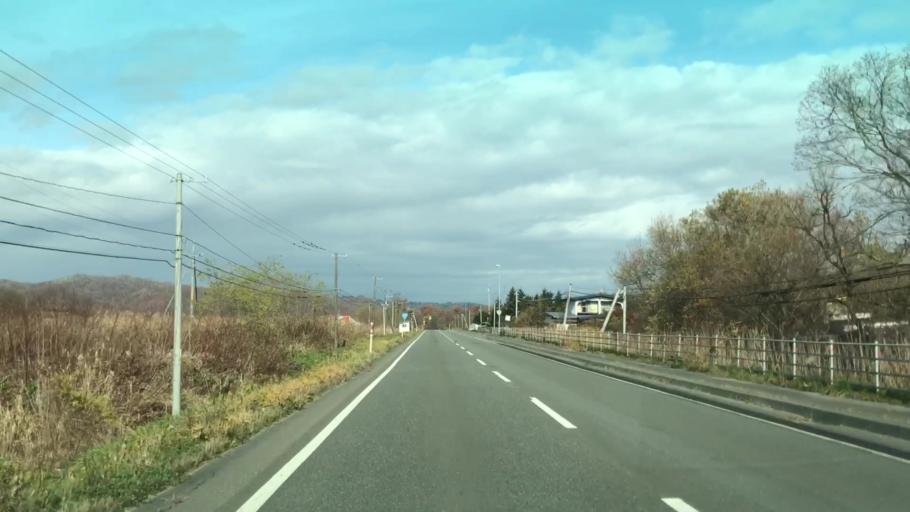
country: JP
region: Hokkaido
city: Shizunai-furukawacho
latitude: 42.6049
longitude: 142.1483
